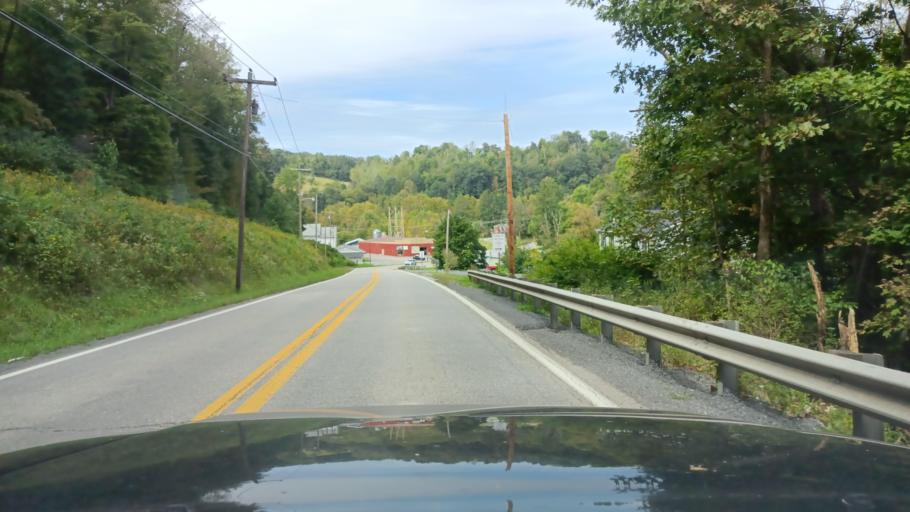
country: US
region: West Virginia
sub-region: Taylor County
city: Grafton
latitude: 39.3464
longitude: -80.0356
